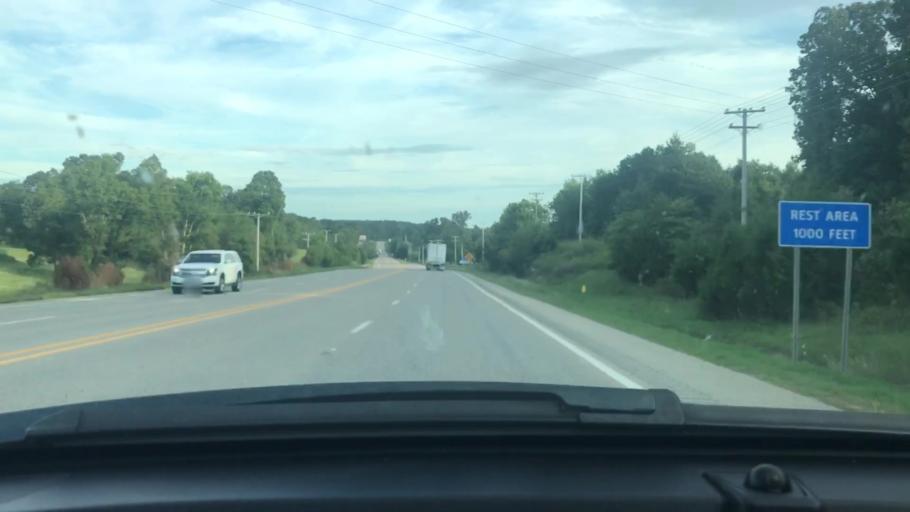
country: US
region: Arkansas
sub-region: Lawrence County
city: Hoxie
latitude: 36.1253
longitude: -91.1543
